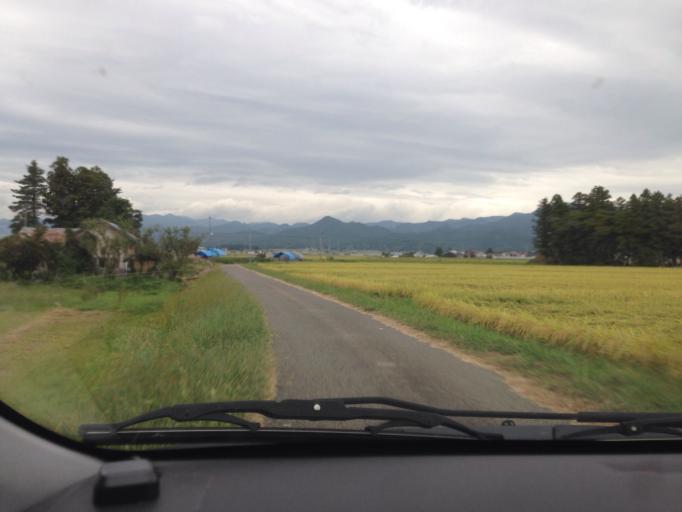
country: JP
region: Fukushima
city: Kitakata
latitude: 37.6322
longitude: 139.9024
